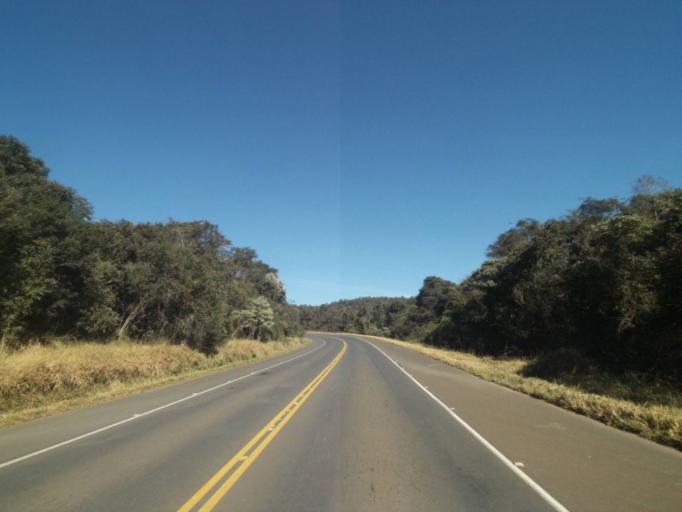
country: BR
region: Parana
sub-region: Tibagi
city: Tibagi
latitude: -24.5512
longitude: -50.4553
